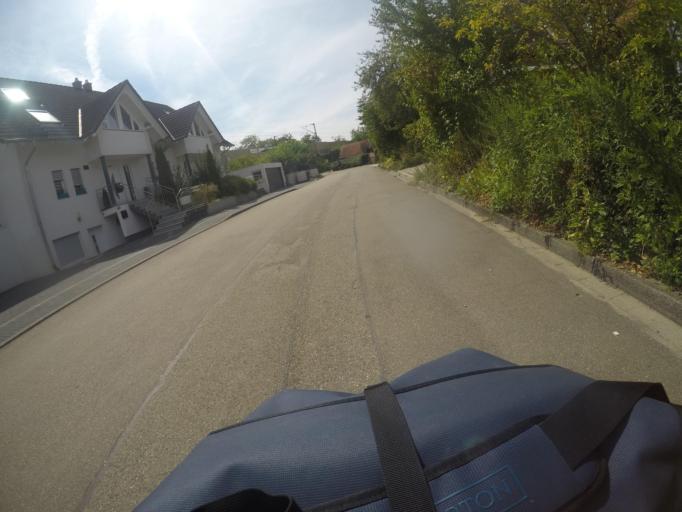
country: DE
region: Baden-Wuerttemberg
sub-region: Freiburg Region
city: Schallstadt
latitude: 47.9574
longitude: 7.7639
